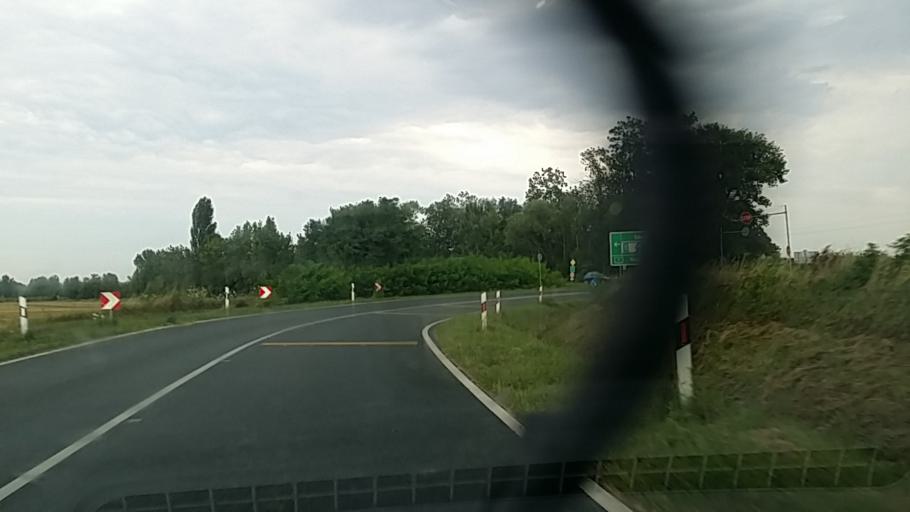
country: HU
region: Zala
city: Zalakomar
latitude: 46.5218
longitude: 17.1477
